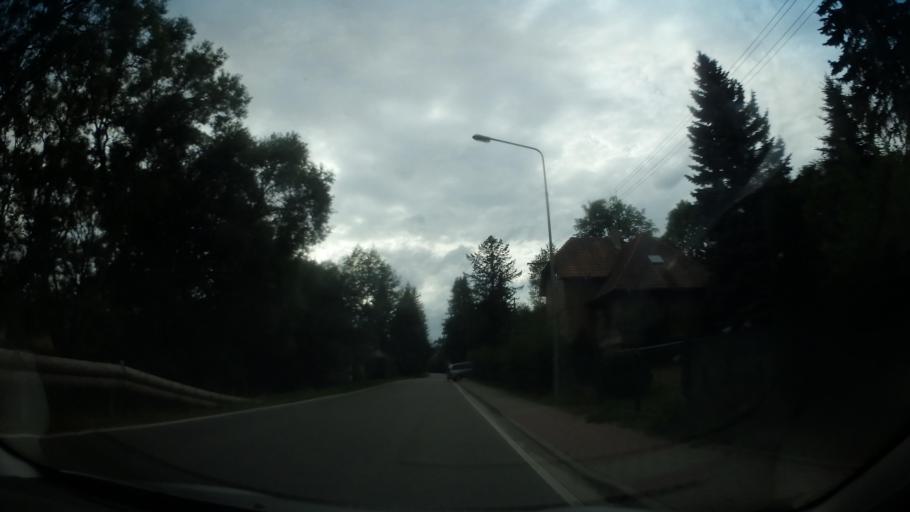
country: CZ
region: Pardubicky
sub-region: Okres Chrudim
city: Nasavrky
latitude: 49.8035
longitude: 15.7484
